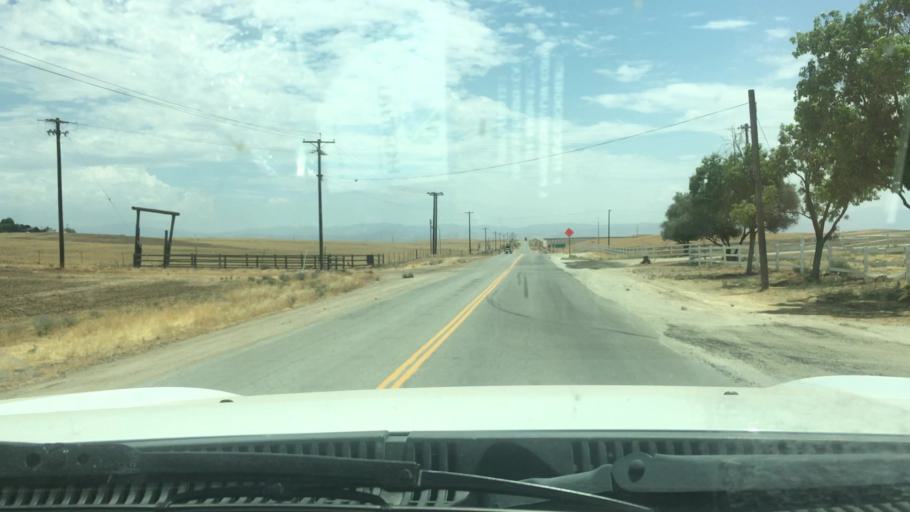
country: US
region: California
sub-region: Kern County
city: McFarland
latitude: 35.6025
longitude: -119.0906
